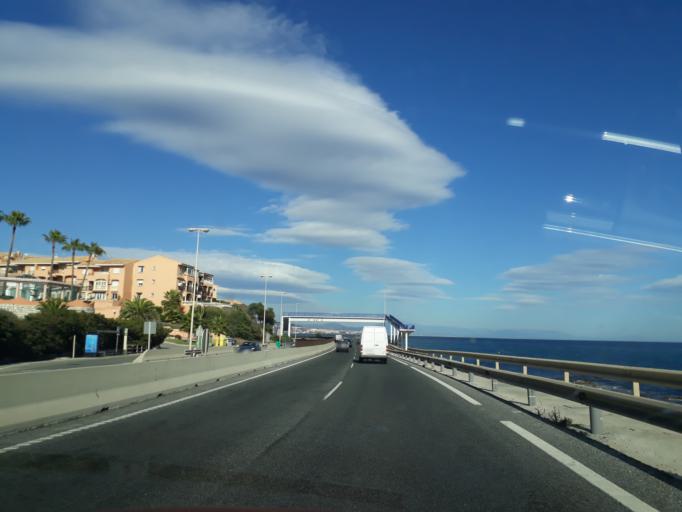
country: ES
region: Andalusia
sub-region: Provincia de Malaga
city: Fuengirola
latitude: 36.5076
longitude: -4.6384
